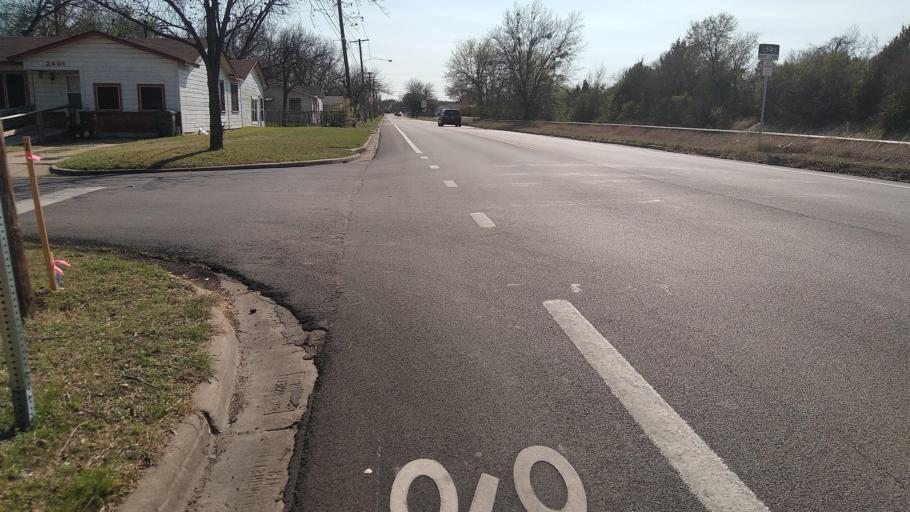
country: US
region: Texas
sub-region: McLennan County
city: Beverly
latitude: 31.5235
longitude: -97.1276
